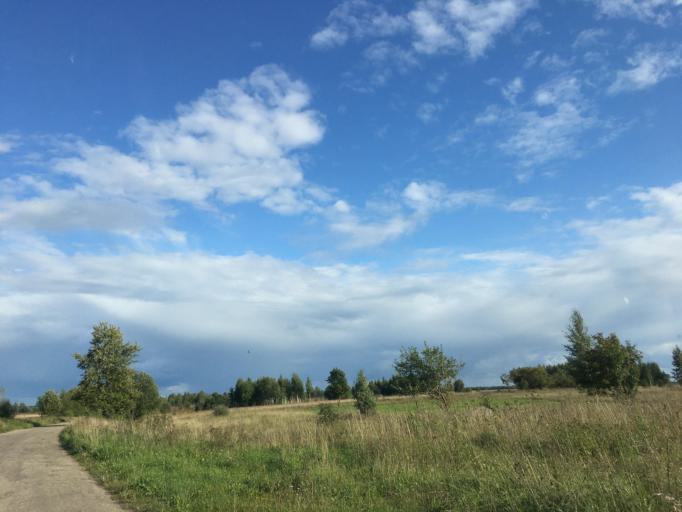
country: RU
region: Pskov
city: Izborsk
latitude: 57.7697
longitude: 27.9834
